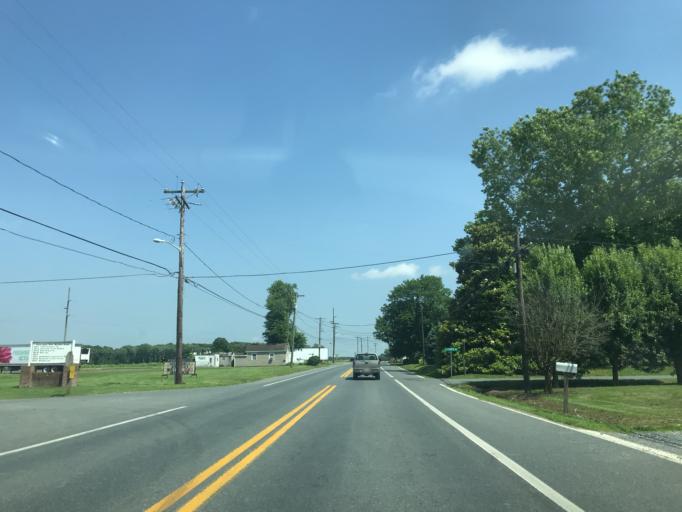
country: US
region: Maryland
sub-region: Dorchester County
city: Hurlock
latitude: 38.5777
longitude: -75.8389
